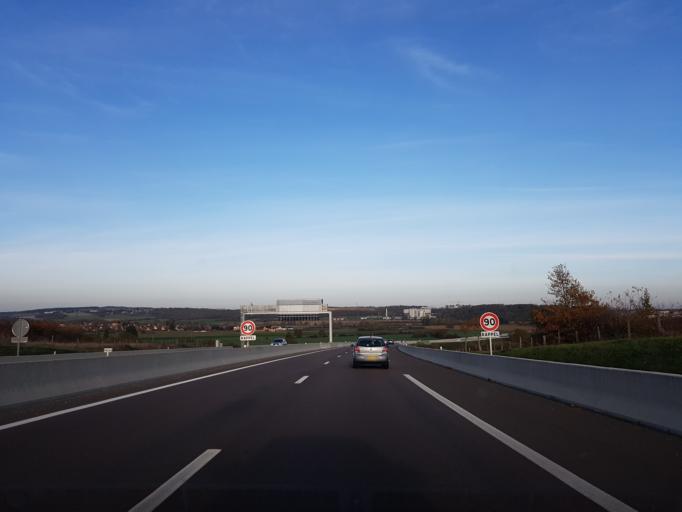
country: FR
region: Bourgogne
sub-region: Departement de la Cote-d'Or
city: Ahuy
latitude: 47.3564
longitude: 5.0191
